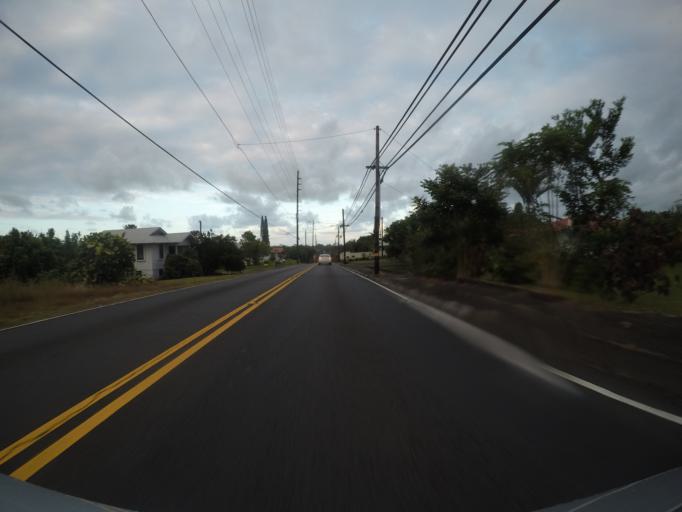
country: US
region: Hawaii
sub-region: Hawaii County
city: Hilo
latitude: 19.6844
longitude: -155.0726
